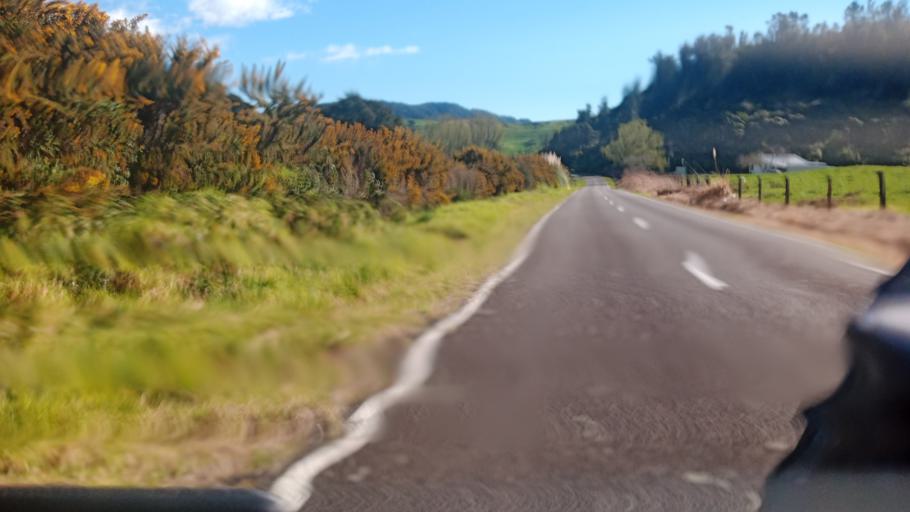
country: NZ
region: Bay of Plenty
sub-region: Opotiki District
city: Opotiki
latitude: -38.0148
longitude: 177.4035
